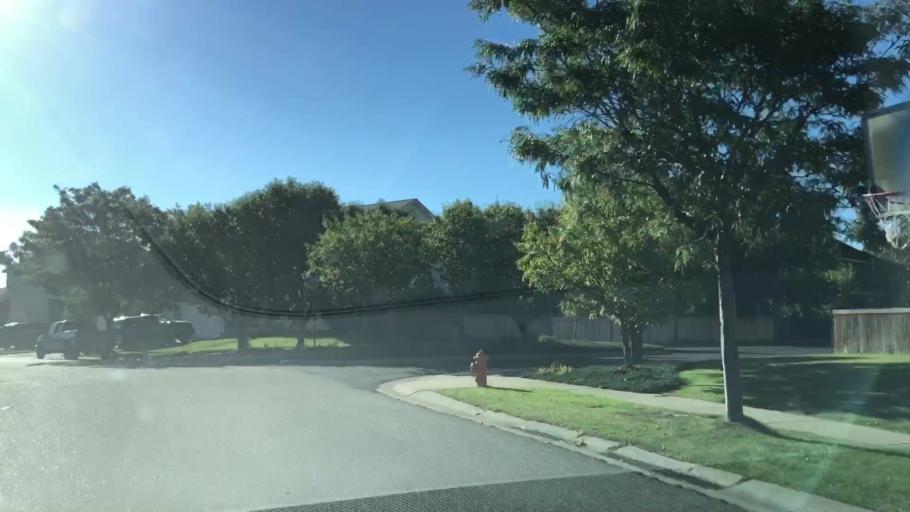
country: US
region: Colorado
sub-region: Larimer County
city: Loveland
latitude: 40.3986
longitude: -105.1353
